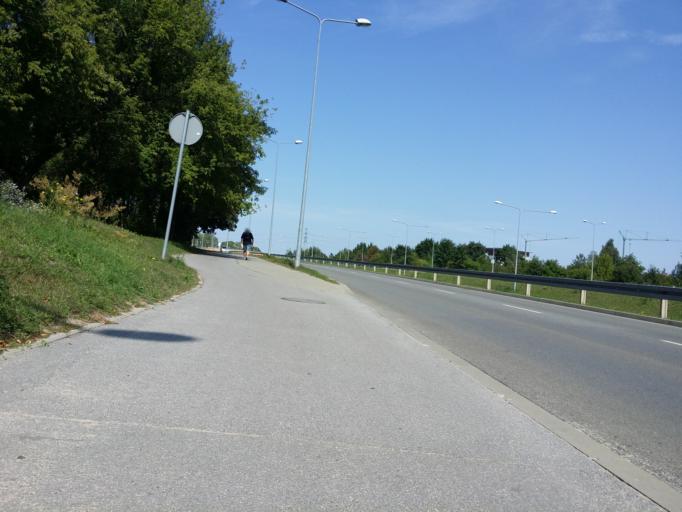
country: PL
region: Masovian Voivodeship
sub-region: Radom
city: Radom
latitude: 51.3731
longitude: 21.1641
